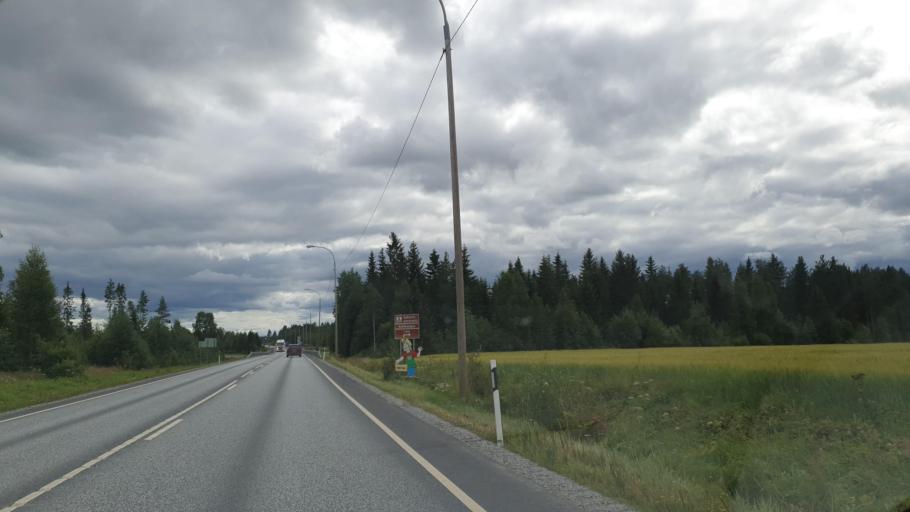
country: FI
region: Northern Savo
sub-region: Ylae-Savo
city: Sonkajaervi
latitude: 63.8780
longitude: 27.4409
